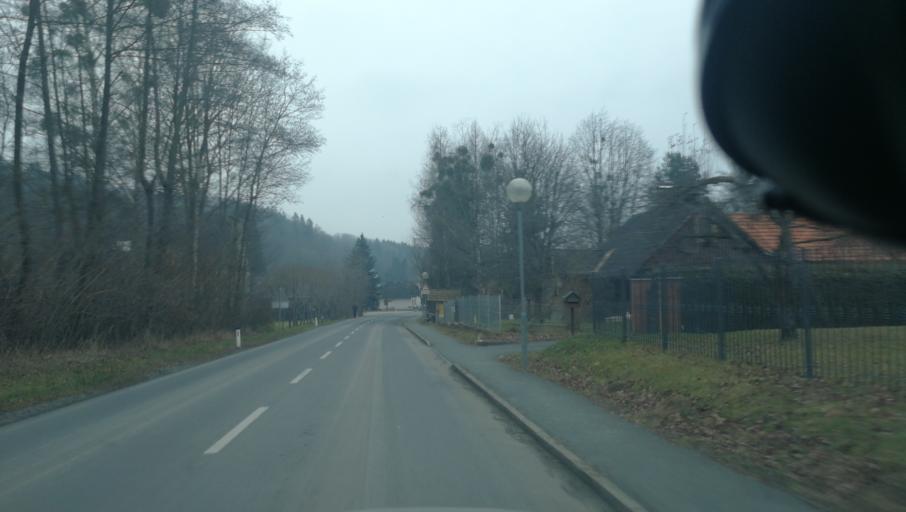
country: AT
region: Styria
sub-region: Politischer Bezirk Deutschlandsberg
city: Greisdorf
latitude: 46.9038
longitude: 15.2411
